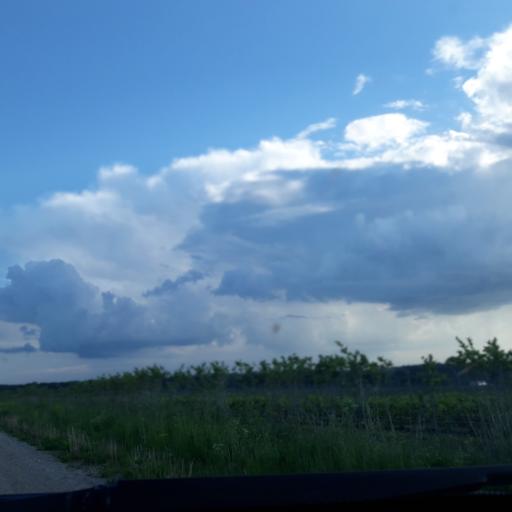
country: LV
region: Talsu Rajons
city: Sabile
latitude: 57.0294
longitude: 22.6165
